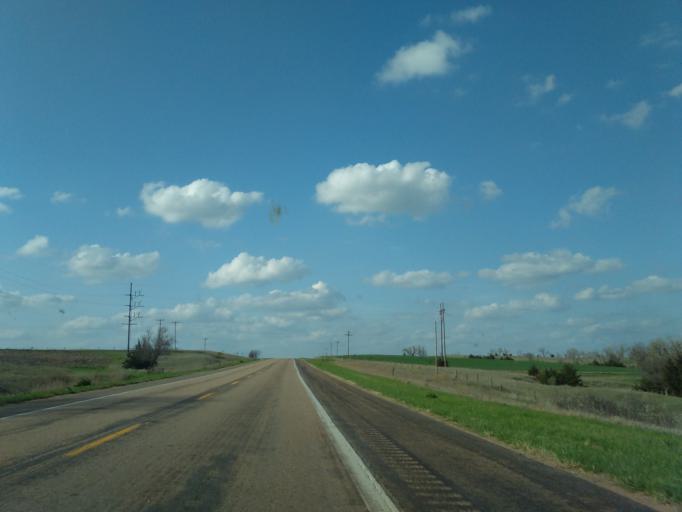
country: US
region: Nebraska
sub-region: Webster County
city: Red Cloud
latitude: 40.1159
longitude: -98.5189
